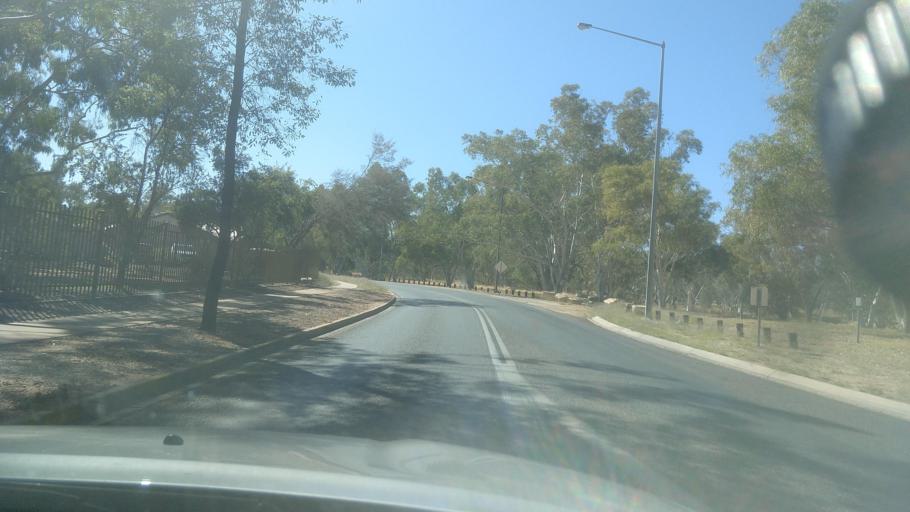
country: AU
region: Northern Territory
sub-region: Alice Springs
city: Alice Springs
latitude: -23.7216
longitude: 133.8727
